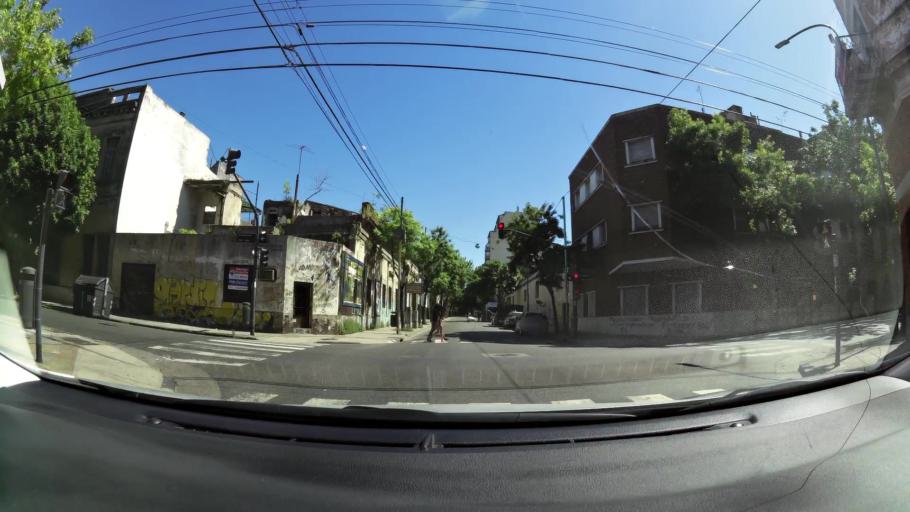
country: AR
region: Buenos Aires F.D.
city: Buenos Aires
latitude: -34.6249
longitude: -58.3872
